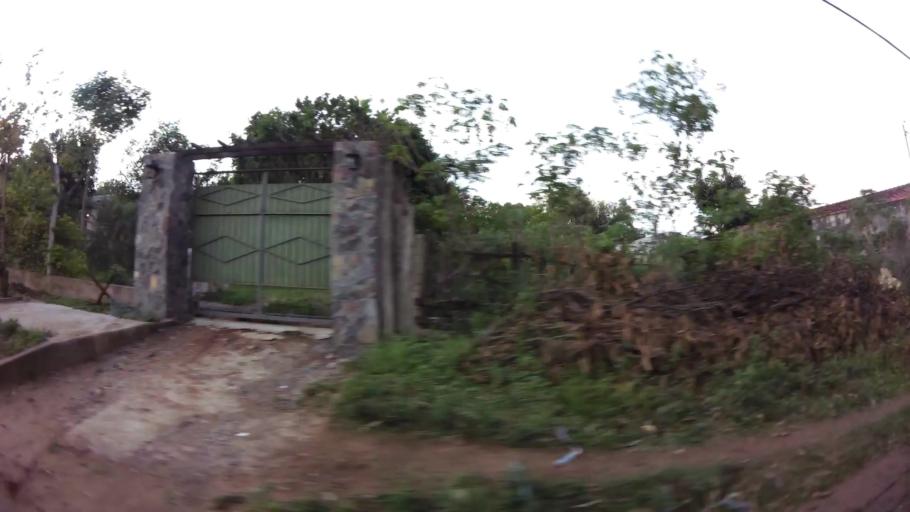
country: PY
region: Central
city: Nemby
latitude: -25.3696
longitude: -57.5285
